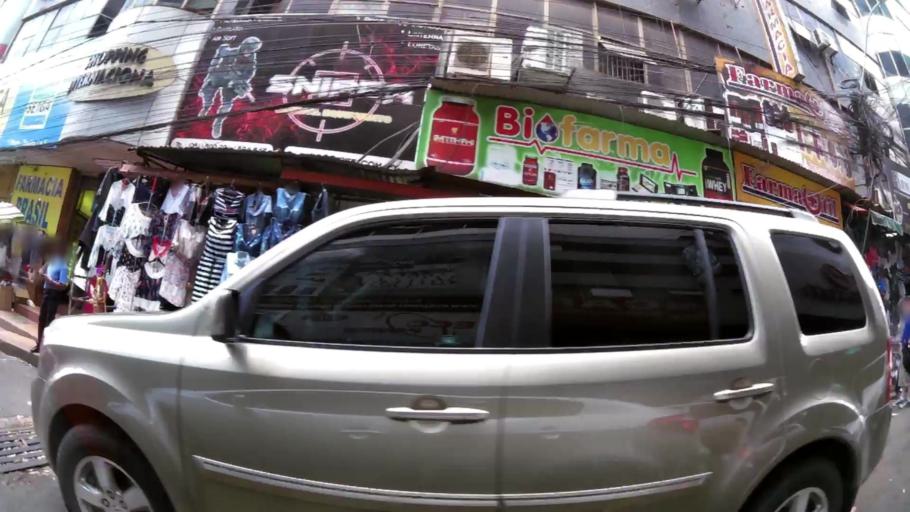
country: PY
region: Alto Parana
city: Ciudad del Este
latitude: -25.5115
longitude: -54.6082
